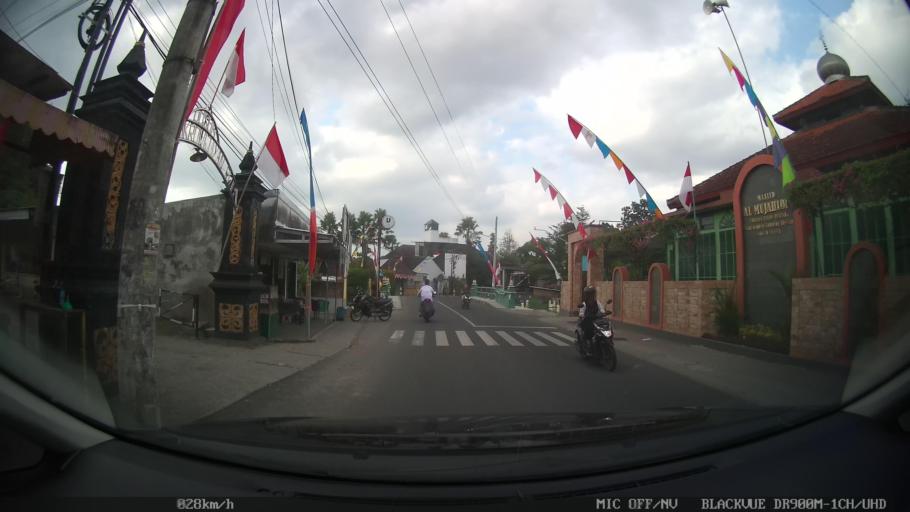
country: ID
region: Daerah Istimewa Yogyakarta
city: Gamping Lor
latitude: -7.7833
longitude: 110.3366
